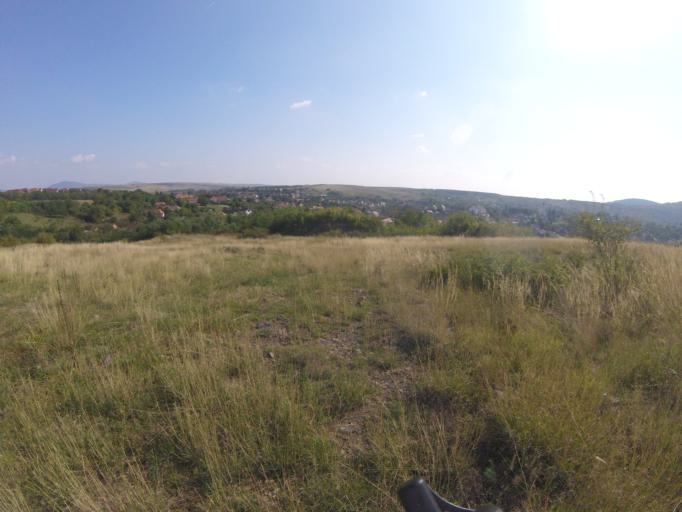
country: HU
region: Nograd
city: Bujak
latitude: 47.8880
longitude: 19.5451
